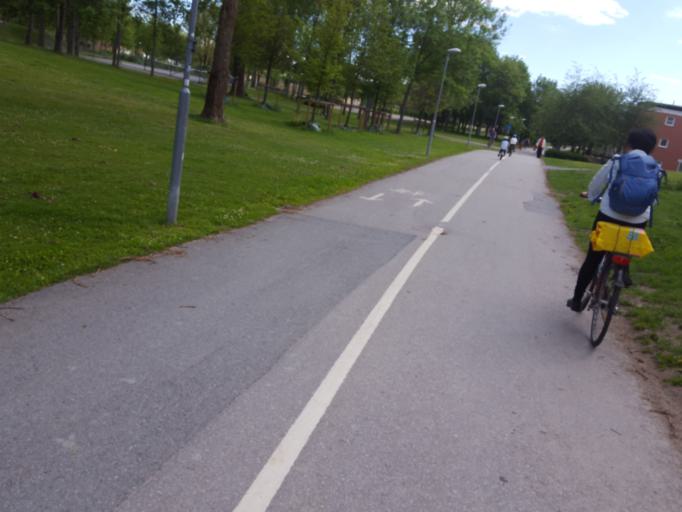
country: SE
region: Uppsala
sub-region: Uppsala Kommun
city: Uppsala
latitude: 59.8761
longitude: 17.6601
